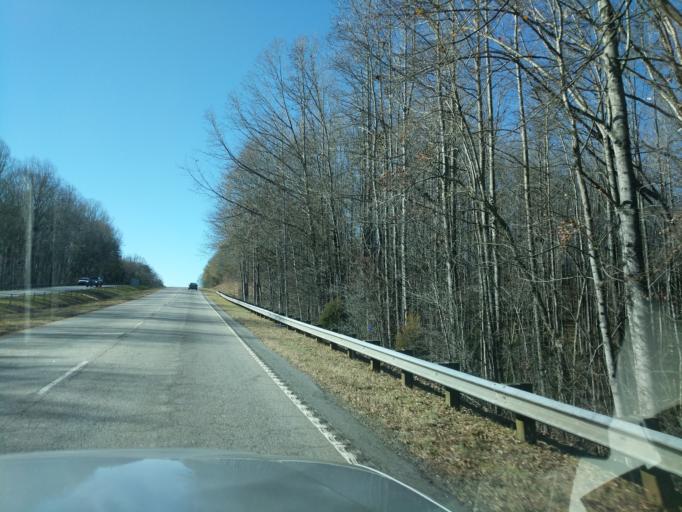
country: US
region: South Carolina
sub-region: Pickens County
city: Central
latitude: 34.7024
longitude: -82.7643
